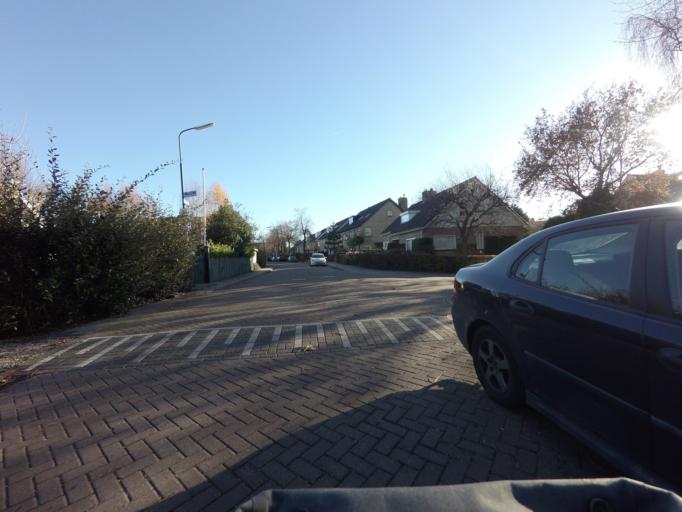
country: NL
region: Utrecht
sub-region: Stichtse Vecht
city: Vreeland
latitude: 52.2476
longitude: 4.9875
